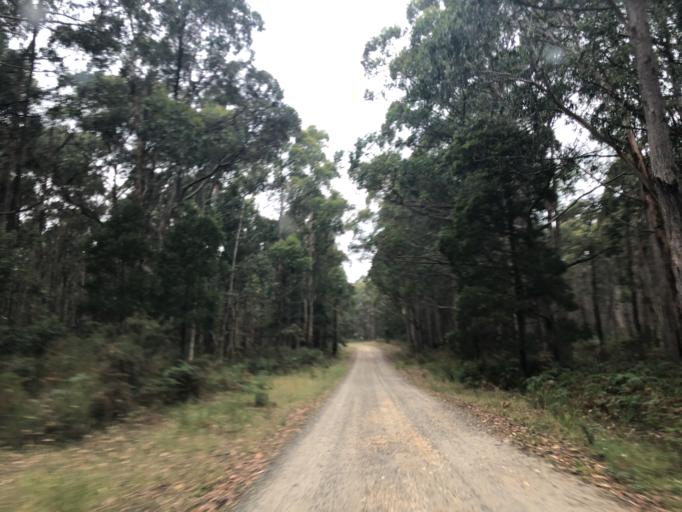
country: AU
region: Victoria
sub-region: Moorabool
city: Bacchus Marsh
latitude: -37.4291
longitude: 144.3487
